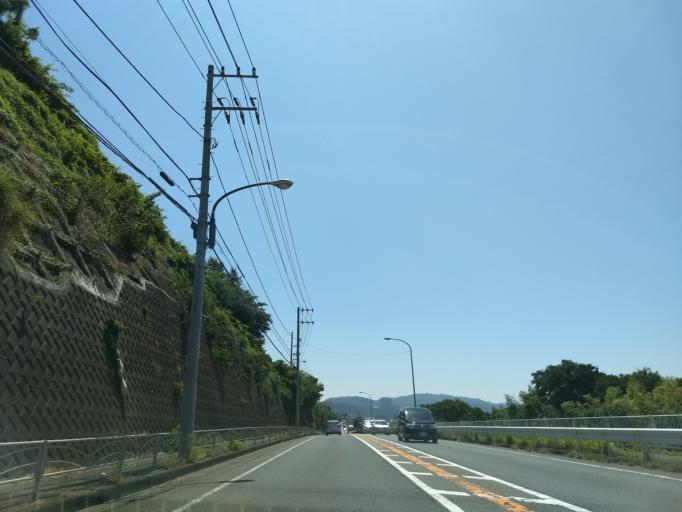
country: JP
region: Kanagawa
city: Odawara
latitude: 35.3534
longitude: 139.1180
